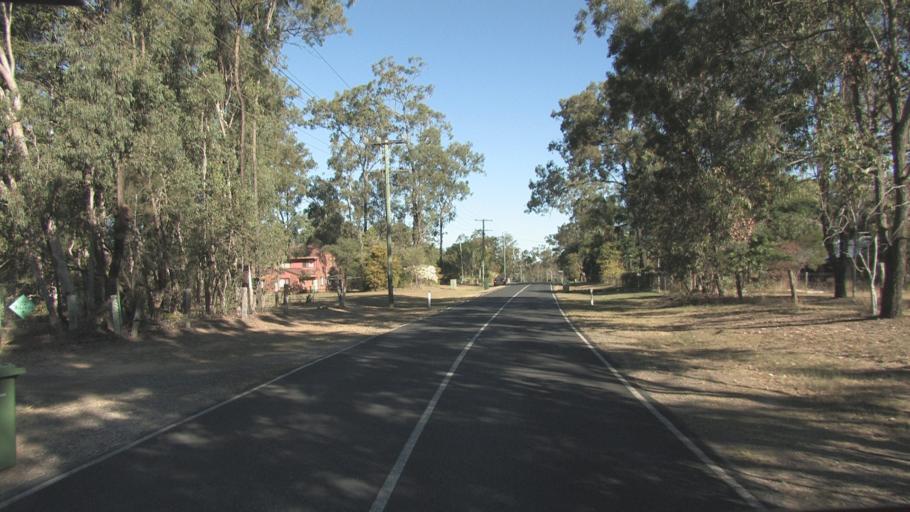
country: AU
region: Queensland
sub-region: Logan
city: Park Ridge South
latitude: -27.7427
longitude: 153.0182
